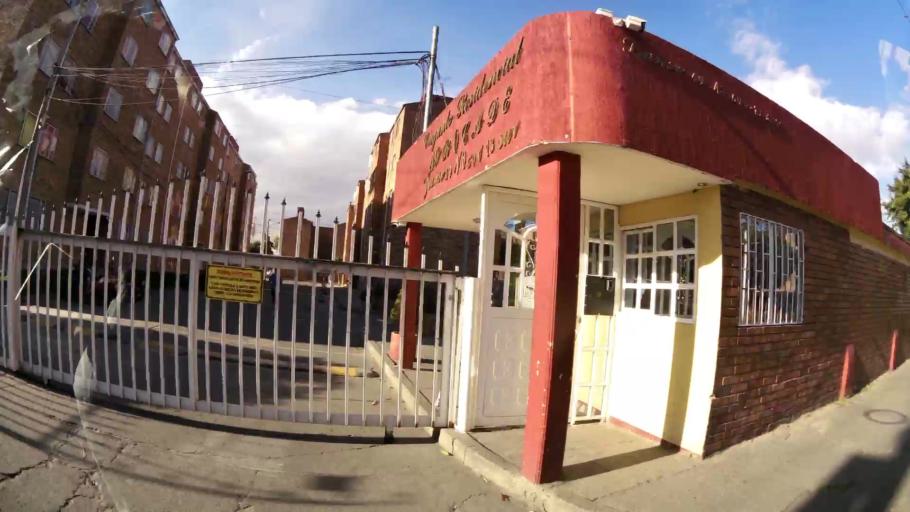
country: CO
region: Cundinamarca
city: Soacha
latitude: 4.5783
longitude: -74.1555
